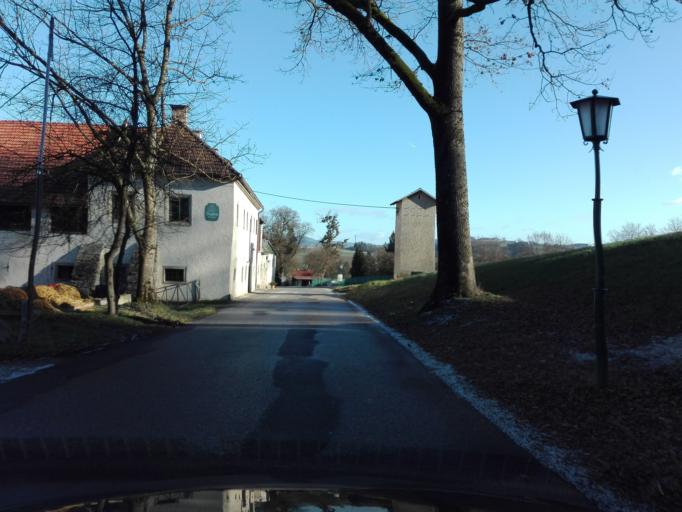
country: AT
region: Upper Austria
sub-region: Politischer Bezirk Perg
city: Bad Kreuzen
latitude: 48.2220
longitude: 14.7776
